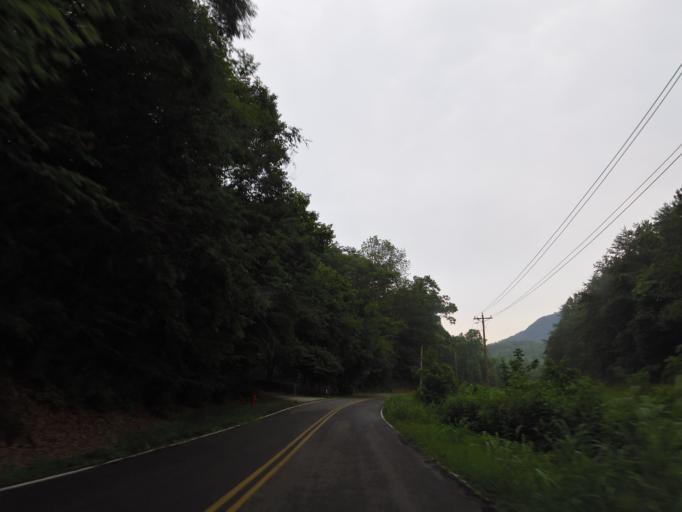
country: US
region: Tennessee
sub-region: Sevier County
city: Seymour
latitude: 35.8473
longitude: -83.6617
